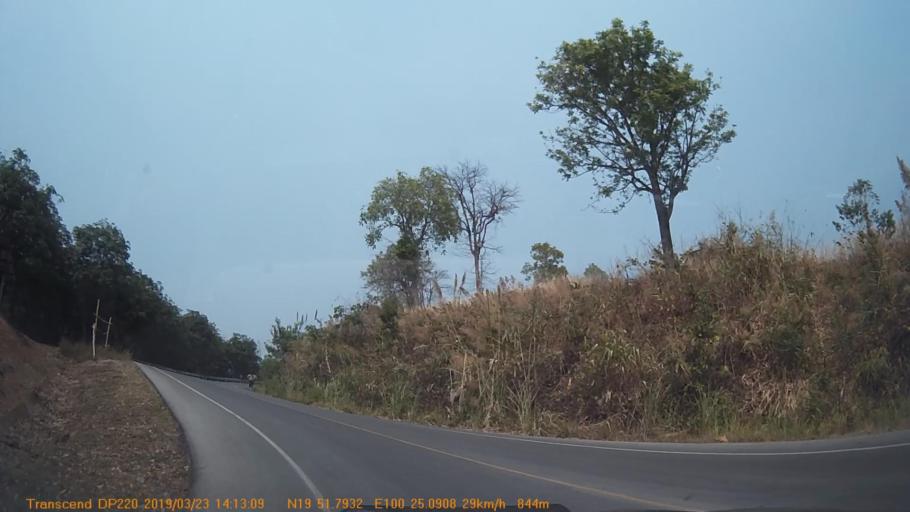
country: TH
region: Chiang Rai
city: Khun Tan
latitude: 19.8633
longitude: 100.4183
